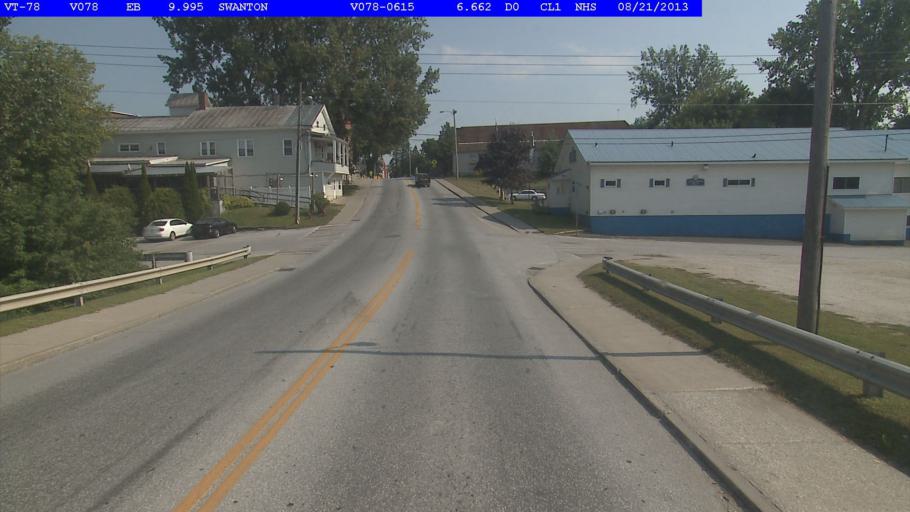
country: US
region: Vermont
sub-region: Franklin County
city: Swanton
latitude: 44.9204
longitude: -73.1270
